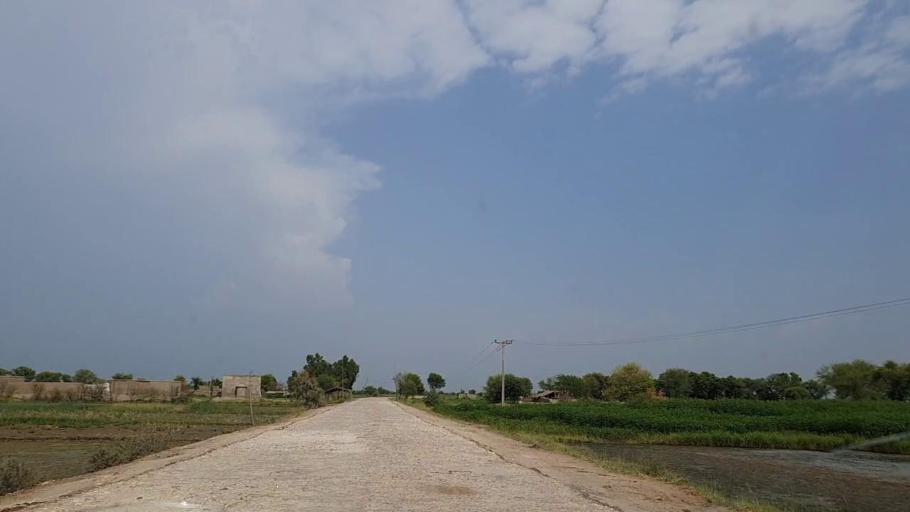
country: PK
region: Sindh
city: Khanpur
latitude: 27.8483
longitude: 69.4458
